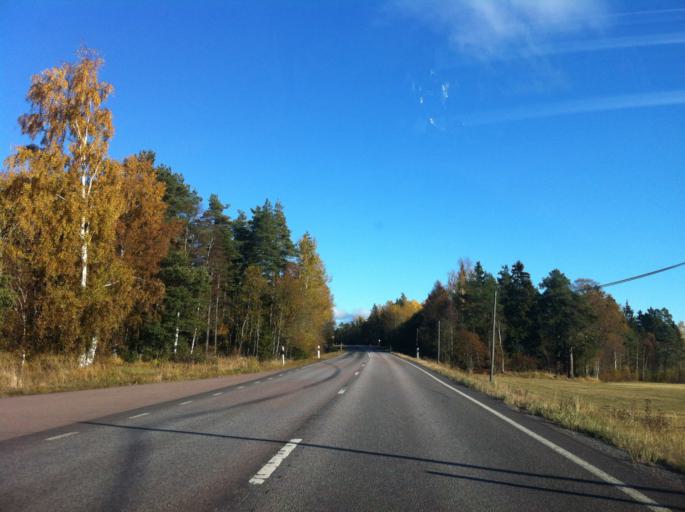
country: SE
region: Uppsala
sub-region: Osthammars Kommun
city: OEsthammar
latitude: 60.3269
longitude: 18.3548
